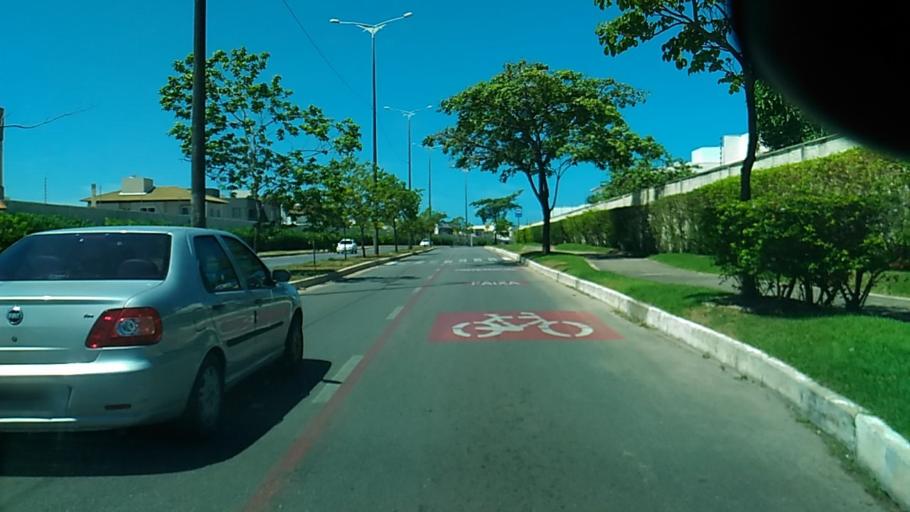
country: BR
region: Paraiba
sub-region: Joao Pessoa
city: Joao Pessoa
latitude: -7.1571
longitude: -34.8190
